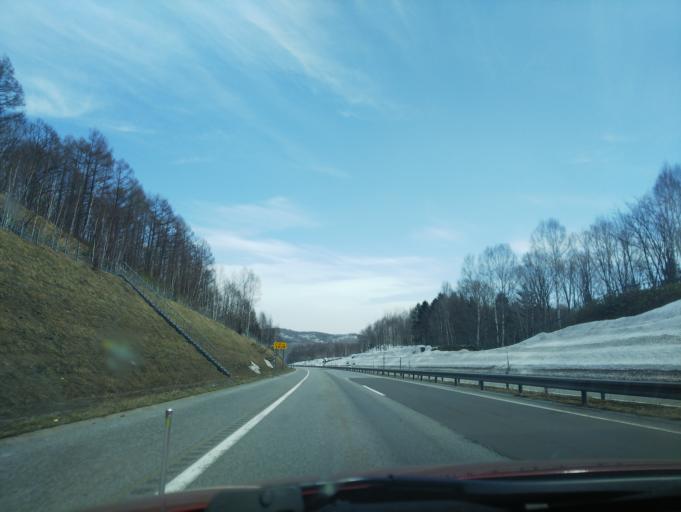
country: JP
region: Hokkaido
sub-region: Asahikawa-shi
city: Asahikawa
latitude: 43.7923
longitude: 142.2708
